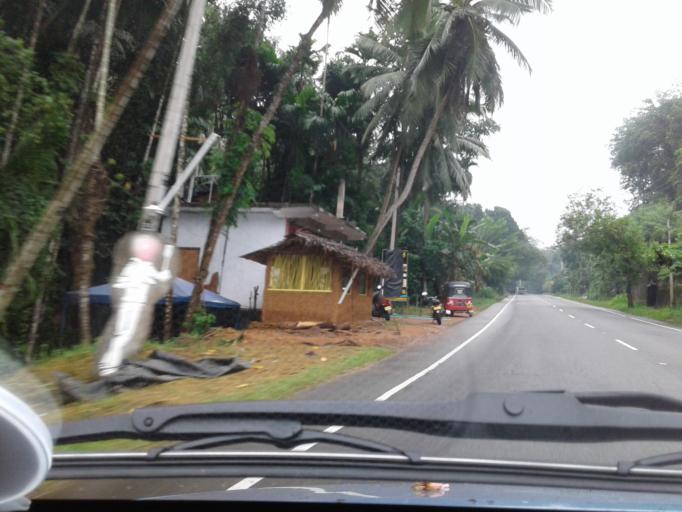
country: LK
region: Central
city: Kadugannawa
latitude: 7.2329
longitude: 80.2517
